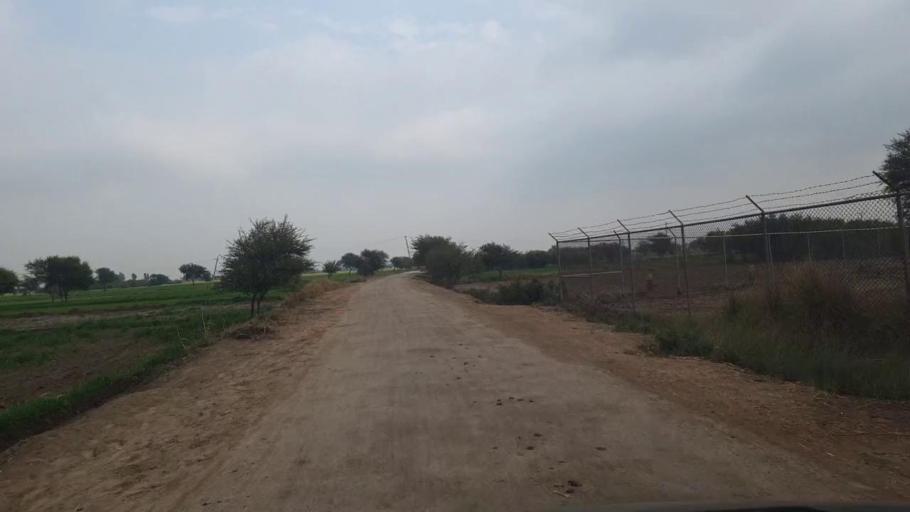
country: PK
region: Sindh
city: Shahdadpur
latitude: 25.8904
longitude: 68.7034
